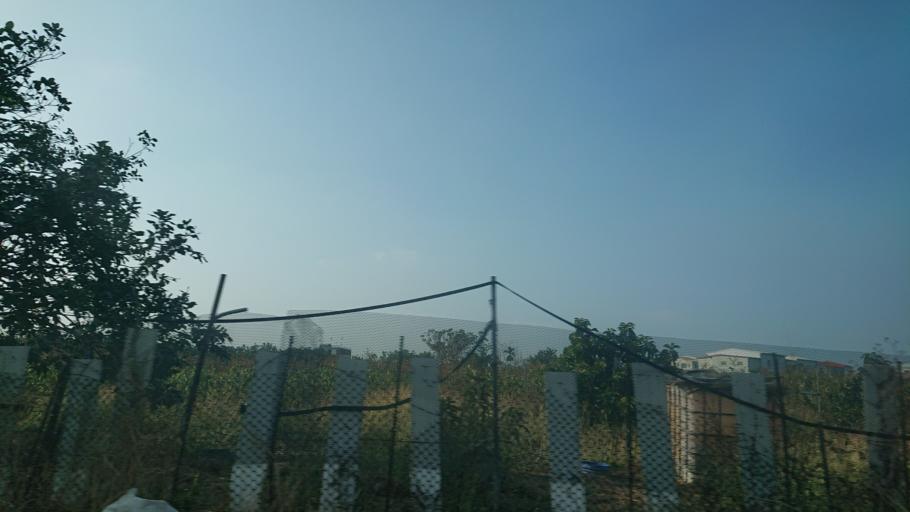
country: TW
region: Taiwan
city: Xinying
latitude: 23.1812
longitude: 120.2655
